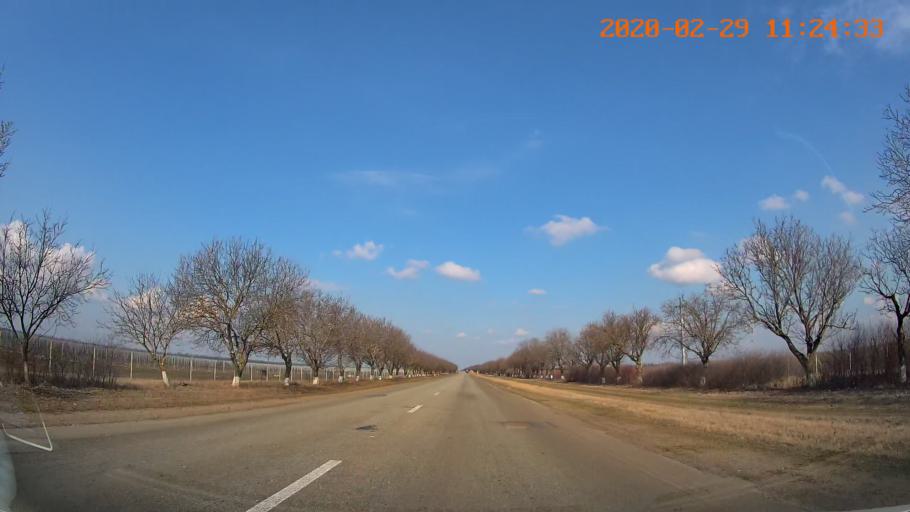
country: MD
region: Telenesti
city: Cocieri
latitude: 47.4255
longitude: 29.1541
